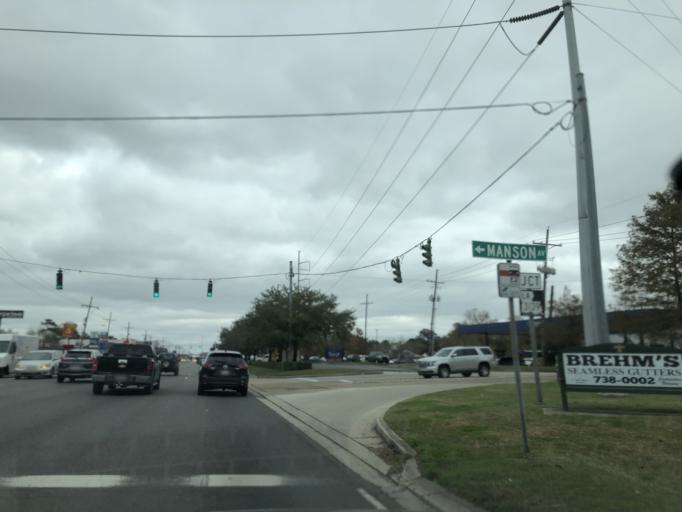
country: US
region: Louisiana
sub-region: Jefferson Parish
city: Metairie Terrace
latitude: 29.9751
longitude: -90.1718
